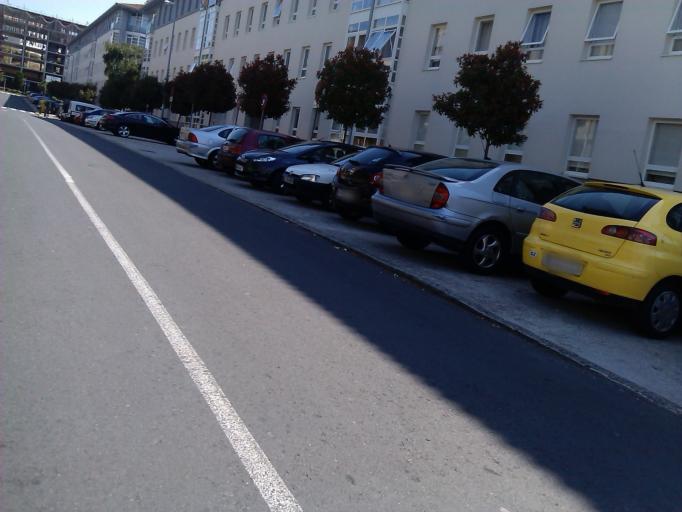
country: ES
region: Galicia
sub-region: Provincia da Coruna
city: Santiago de Compostela
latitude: 42.8824
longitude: -8.5328
